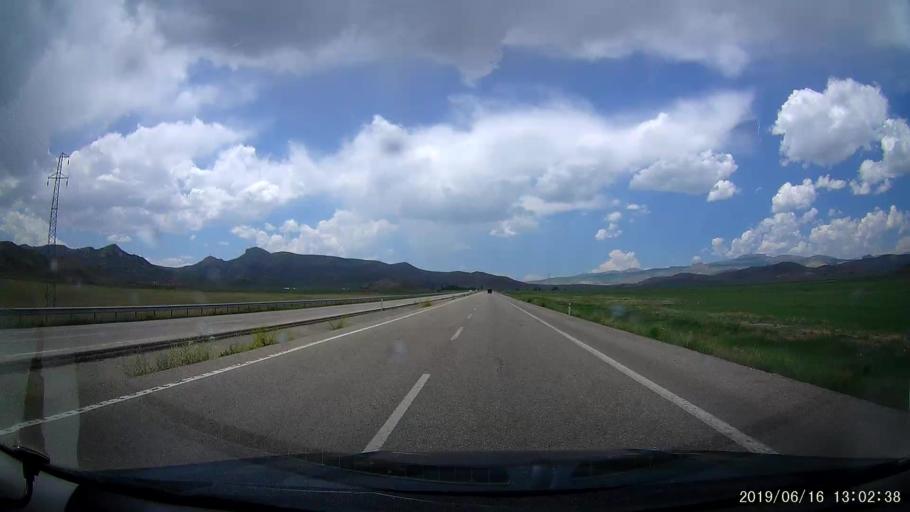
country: TR
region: Agri
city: Sulucem
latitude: 39.5758
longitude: 43.8107
